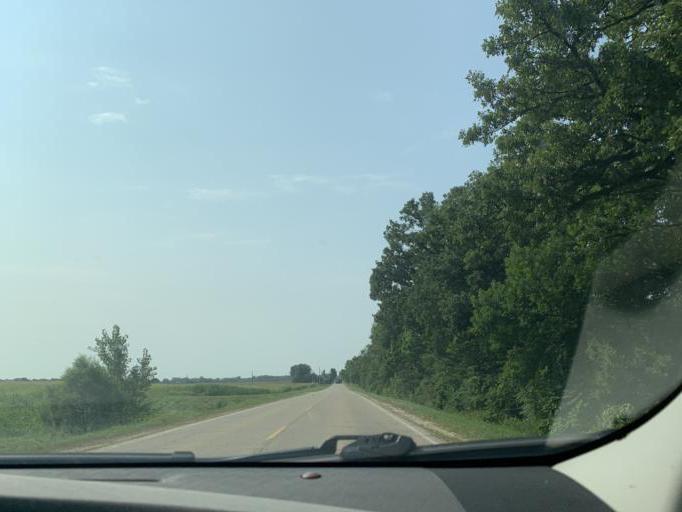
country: US
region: Illinois
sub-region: Whiteside County
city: Sterling
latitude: 41.8055
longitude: -89.7423
